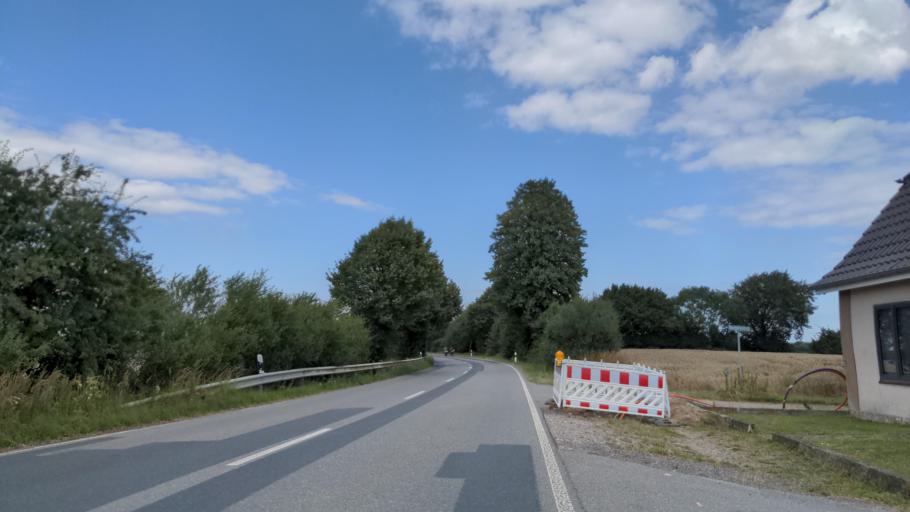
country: DE
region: Schleswig-Holstein
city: Beschendorf
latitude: 54.1679
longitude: 10.8726
